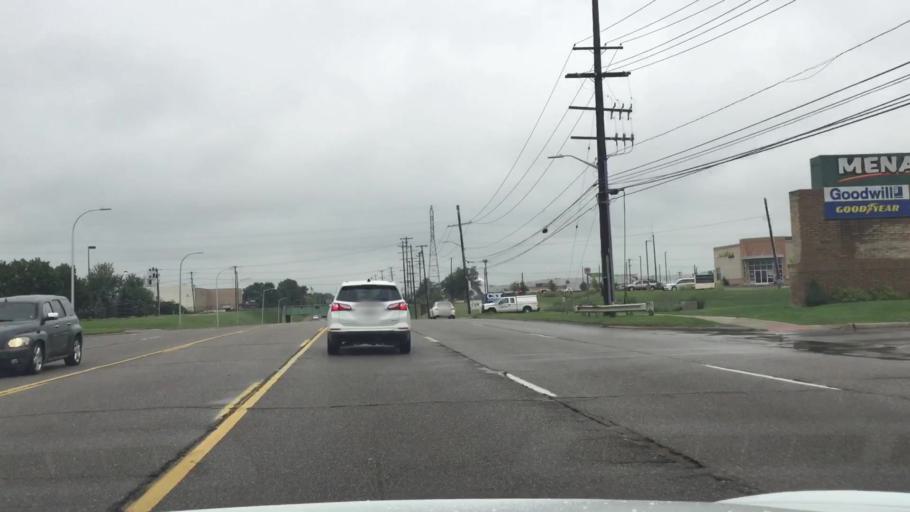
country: US
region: Michigan
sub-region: Wayne County
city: Livonia
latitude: 42.3791
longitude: -83.3336
